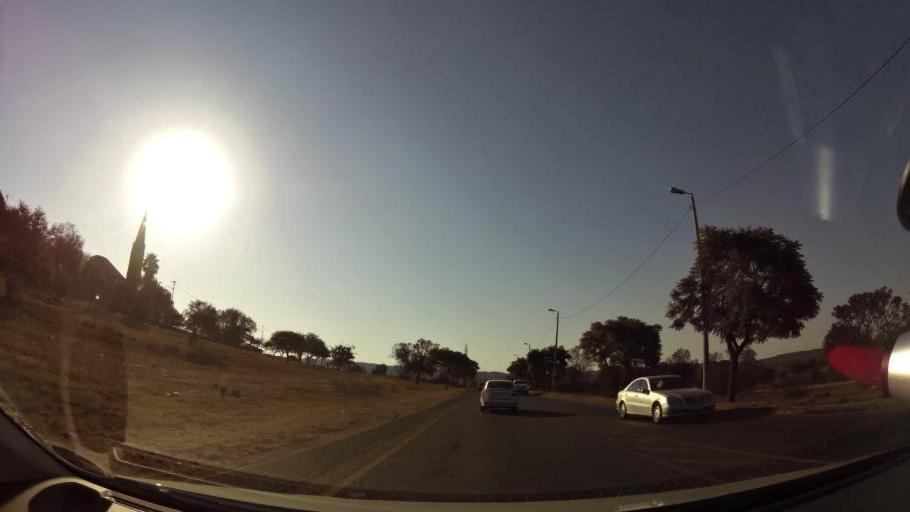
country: ZA
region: Gauteng
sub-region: City of Tshwane Metropolitan Municipality
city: Pretoria
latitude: -25.7533
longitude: 28.1333
